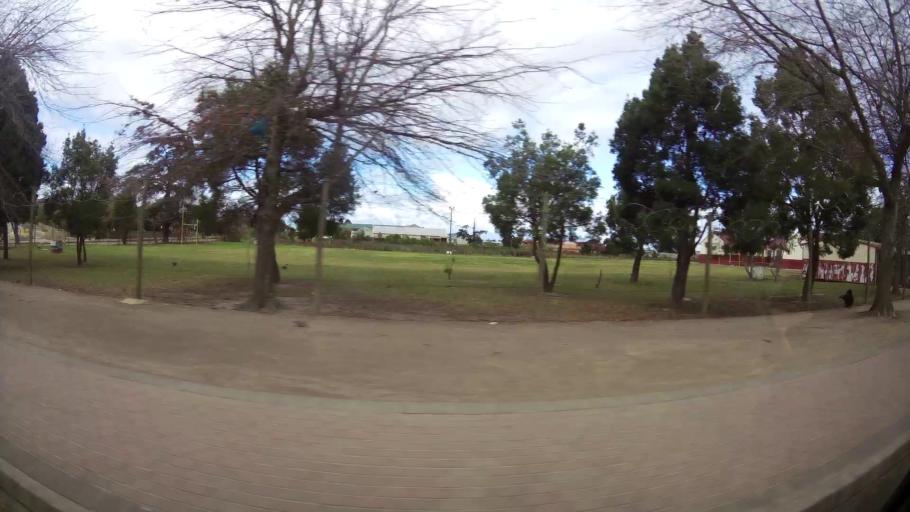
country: ZA
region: Western Cape
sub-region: Eden District Municipality
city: George
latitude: -33.9651
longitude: 22.4758
